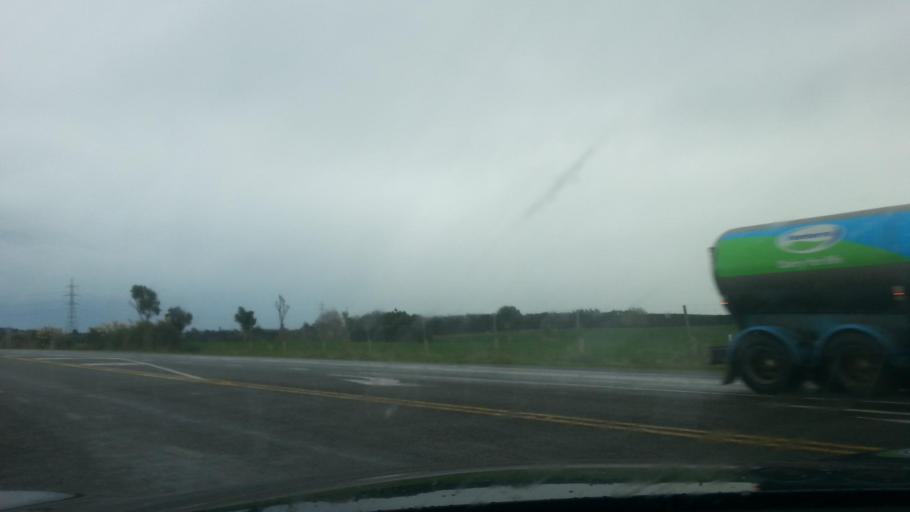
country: NZ
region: Southland
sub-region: Invercargill City
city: Invercargill
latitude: -46.3471
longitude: 168.4161
